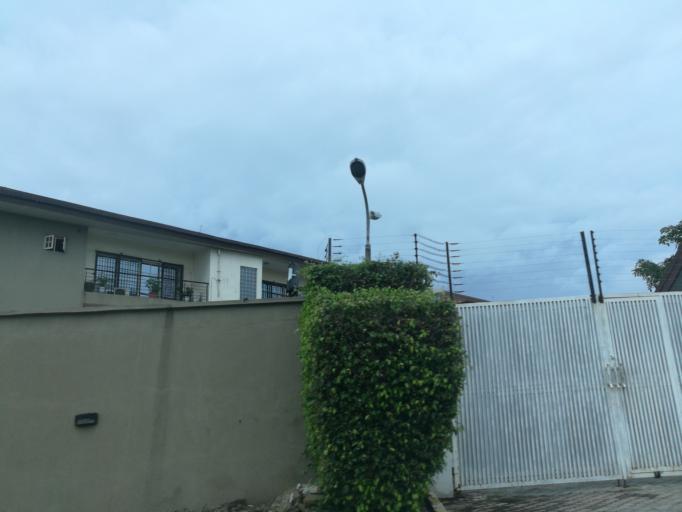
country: NG
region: Lagos
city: Ikoyi
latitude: 6.4394
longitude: 3.4756
